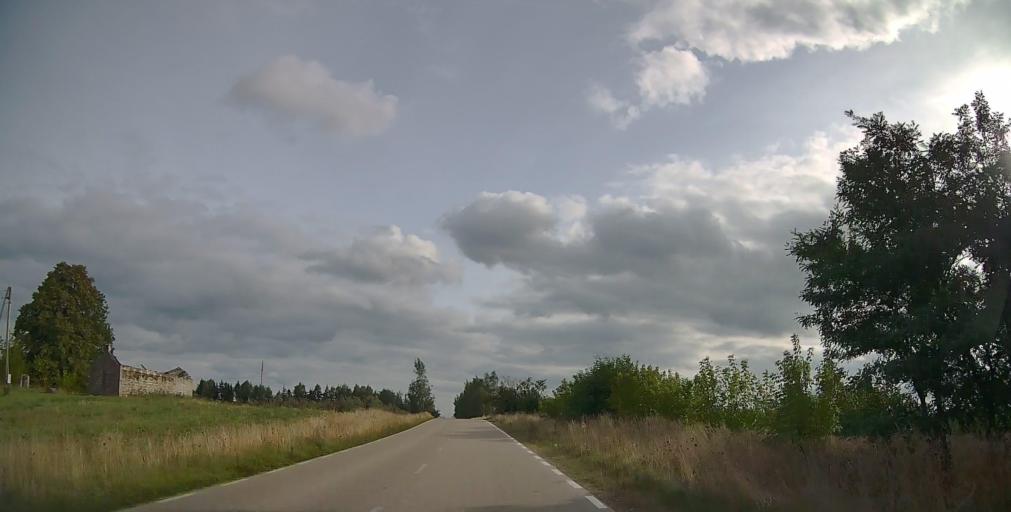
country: PL
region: Masovian Voivodeship
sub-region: Powiat grojecki
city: Goszczyn
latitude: 51.7560
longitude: 20.9025
